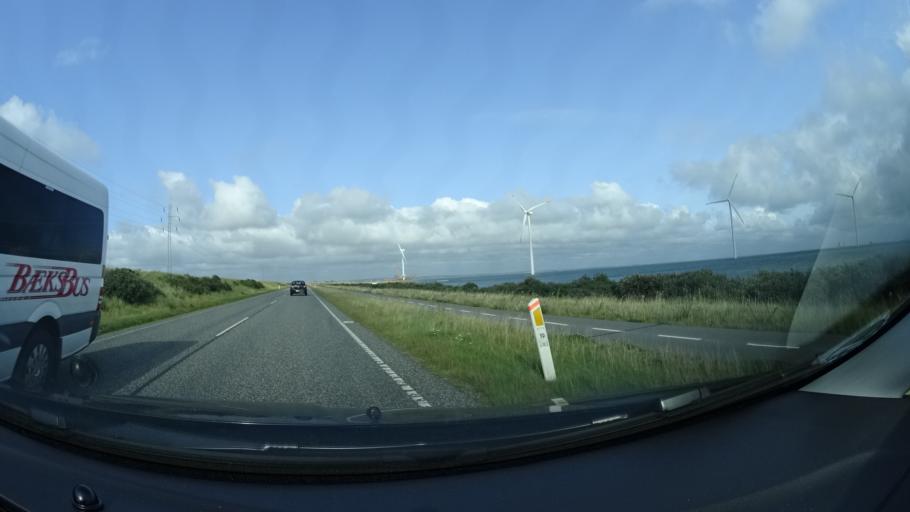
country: DK
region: Central Jutland
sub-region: Lemvig Kommune
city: Thyboron
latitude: 56.6686
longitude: 8.2076
